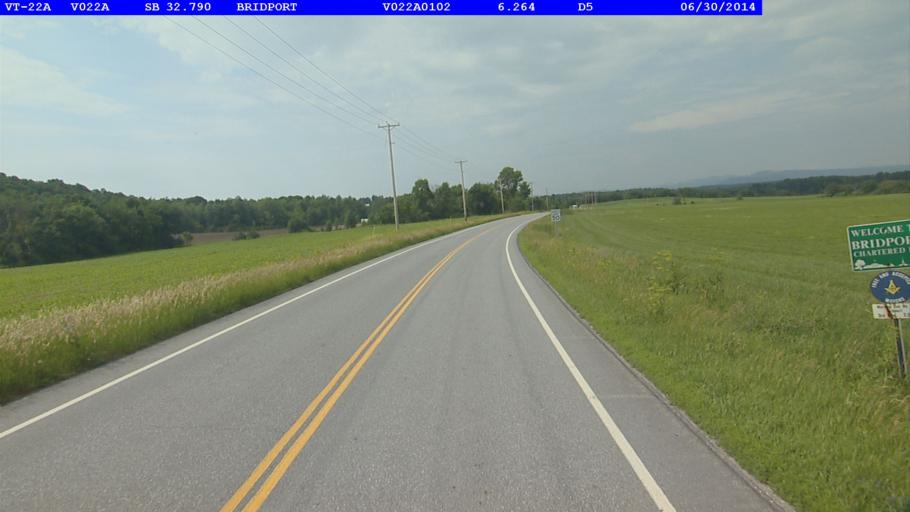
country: US
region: Vermont
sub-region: Addison County
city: Middlebury (village)
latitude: 44.0294
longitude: -73.3078
